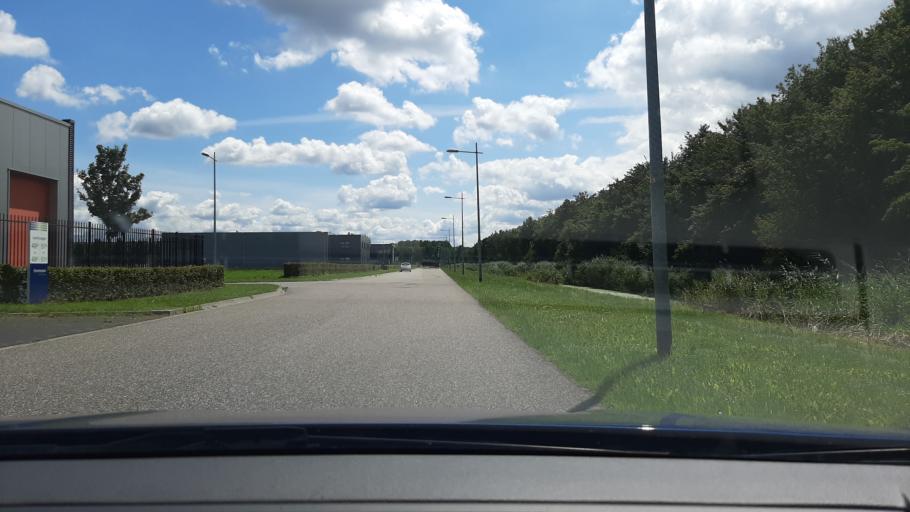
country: NL
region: Flevoland
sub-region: Gemeente Zeewolde
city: Zeewolde
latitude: 52.3498
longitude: 5.4886
